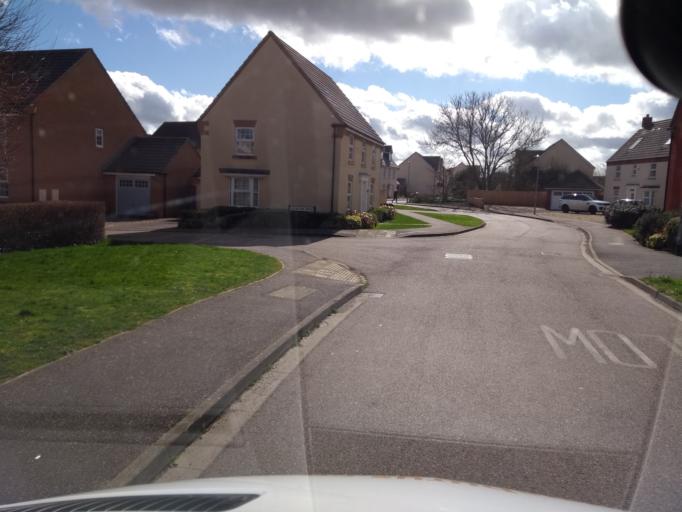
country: GB
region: England
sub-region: Somerset
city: Creech Saint Michael
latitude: 51.0288
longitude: -3.0454
